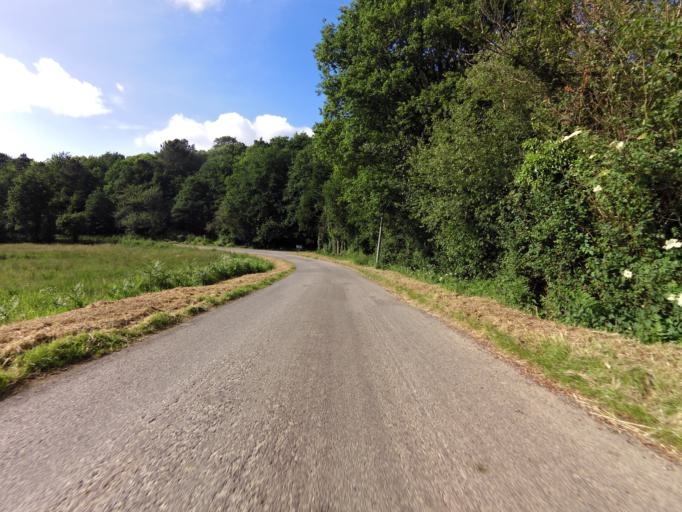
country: FR
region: Brittany
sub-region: Departement du Morbihan
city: Molac
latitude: 47.7187
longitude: -2.4140
